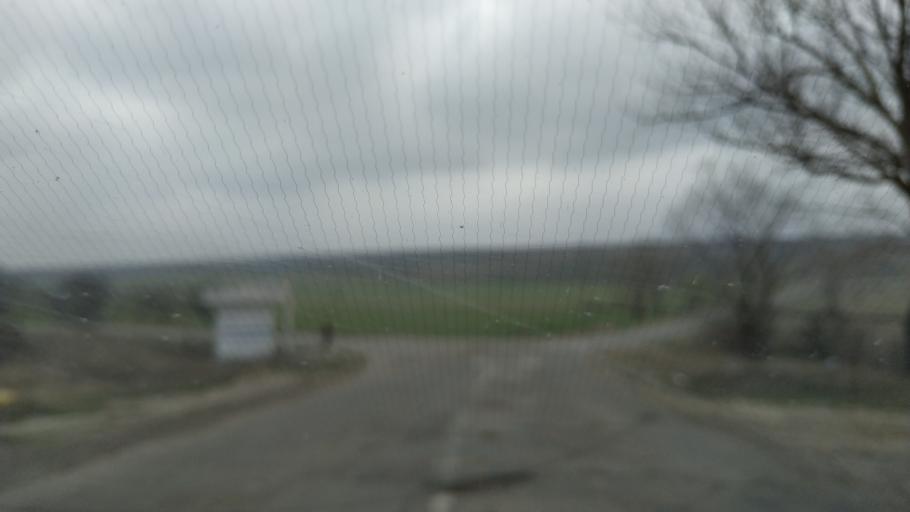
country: MD
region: Gagauzia
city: Bugeac
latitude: 46.3358
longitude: 28.7601
